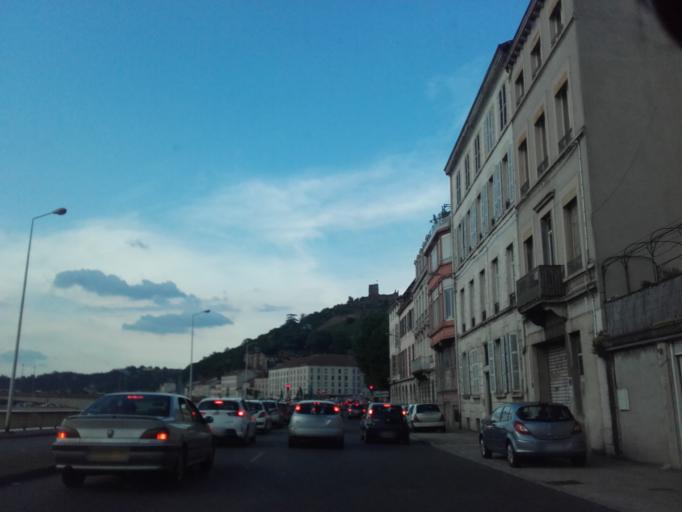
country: FR
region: Rhone-Alpes
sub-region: Departement de l'Isere
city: Vienne
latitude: 45.5263
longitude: 4.8725
